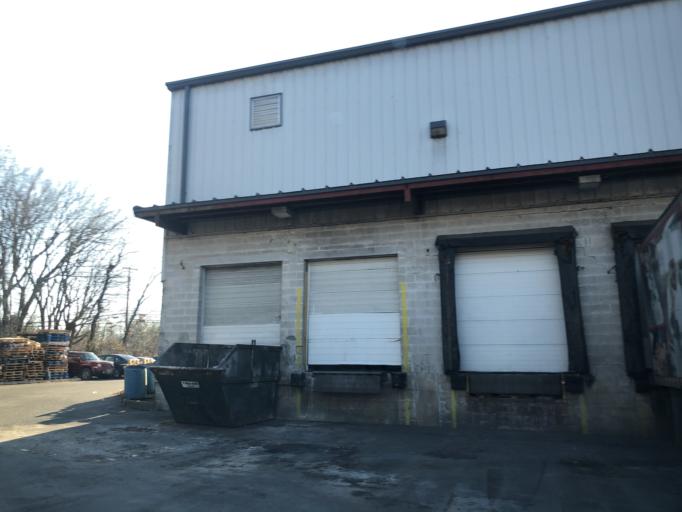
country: US
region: New Jersey
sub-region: Salem County
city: Carneys Point
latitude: 39.7037
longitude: -75.4404
